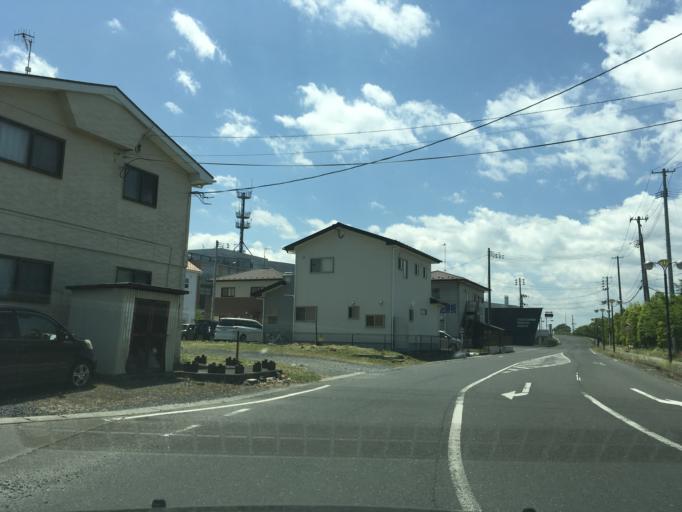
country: JP
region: Miyagi
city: Wakuya
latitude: 38.6824
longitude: 141.2084
